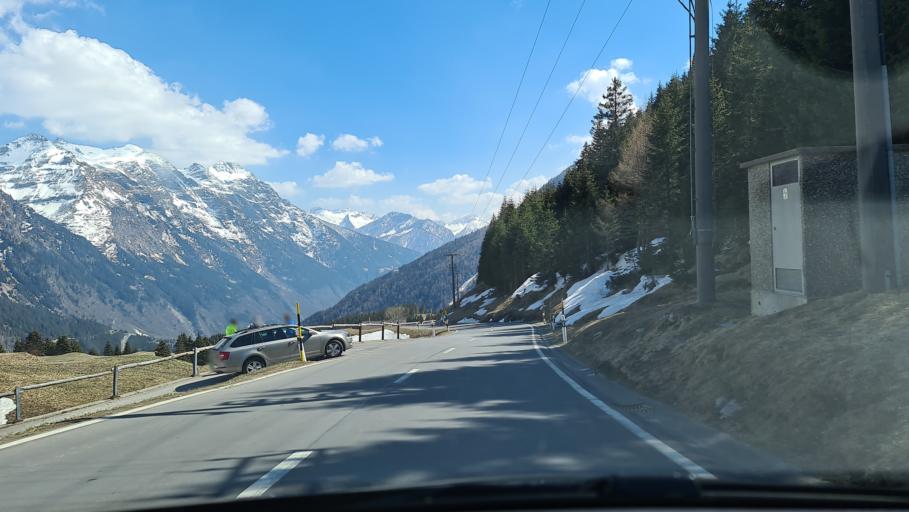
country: CH
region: Grisons
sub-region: Moesa District
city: Mesocco
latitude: 46.4431
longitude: 9.2023
